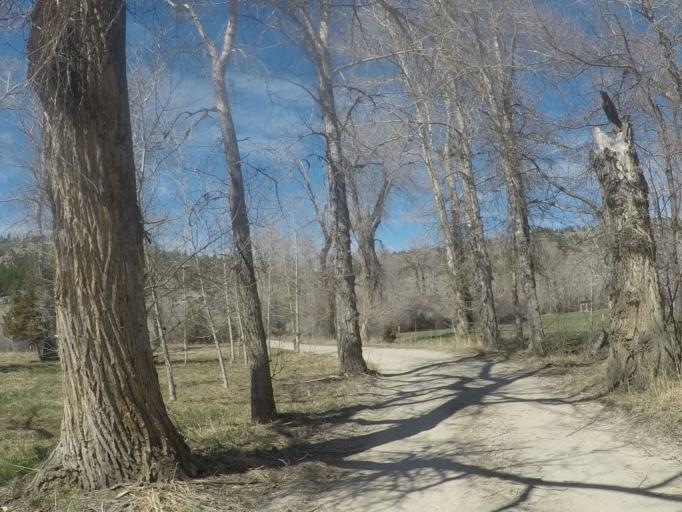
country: US
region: Montana
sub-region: Stillwater County
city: Columbus
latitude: 45.5829
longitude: -109.3312
